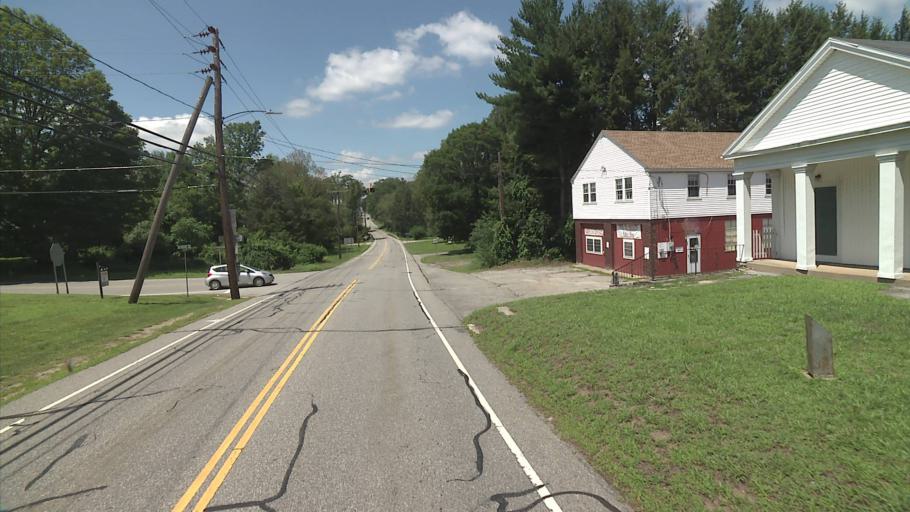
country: US
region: Connecticut
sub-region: Windham County
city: Windham
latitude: 41.6985
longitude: -72.0821
